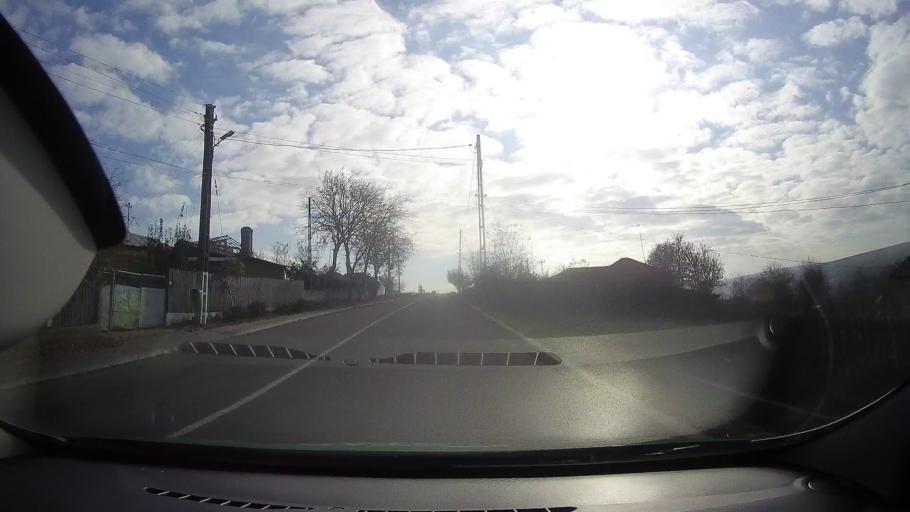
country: RO
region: Tulcea
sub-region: Comuna Bestepe
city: Bestepe
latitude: 45.0846
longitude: 29.0207
